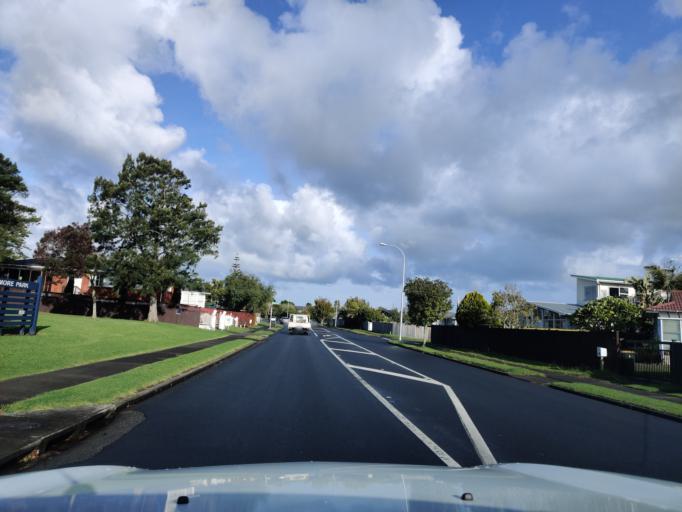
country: NZ
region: Auckland
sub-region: Auckland
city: Pakuranga
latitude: -36.9092
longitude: 174.8984
